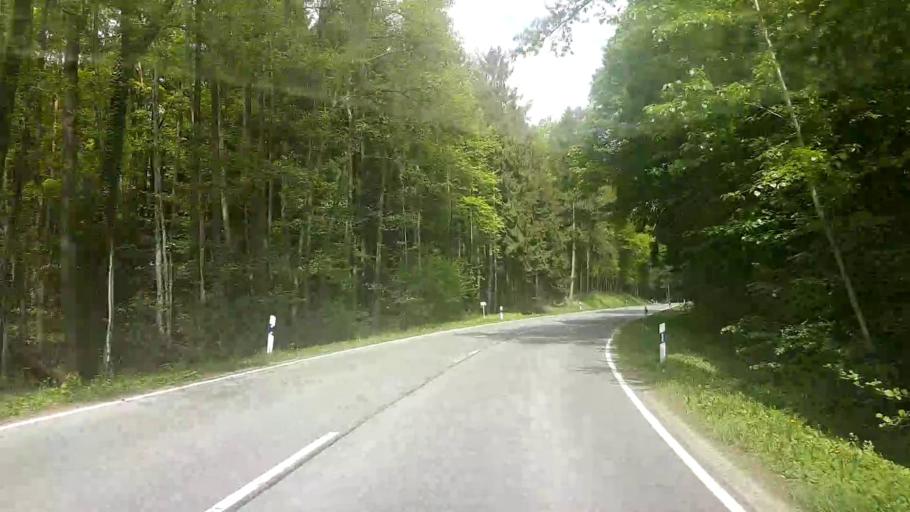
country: DE
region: Bavaria
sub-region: Upper Franconia
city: Lichtenfels
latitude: 50.1659
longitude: 11.0518
